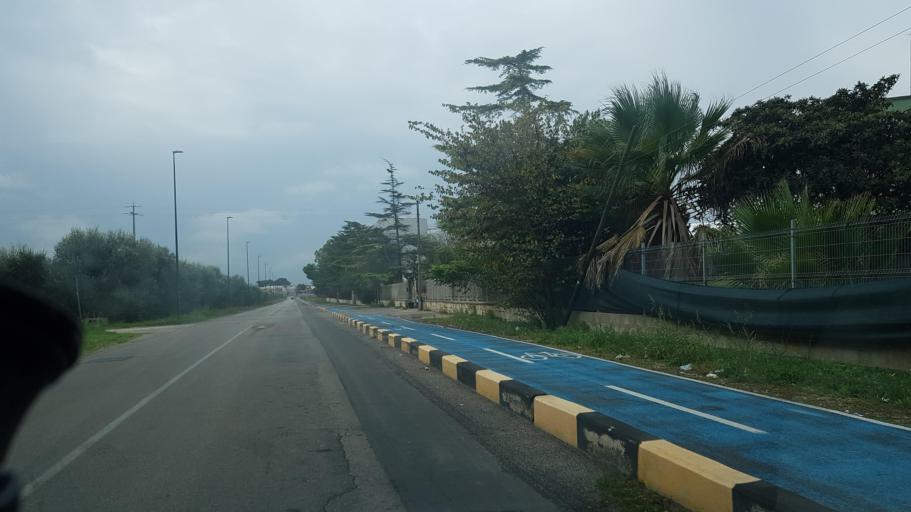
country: IT
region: Apulia
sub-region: Provincia di Lecce
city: Guagnano
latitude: 40.4101
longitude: 17.9570
